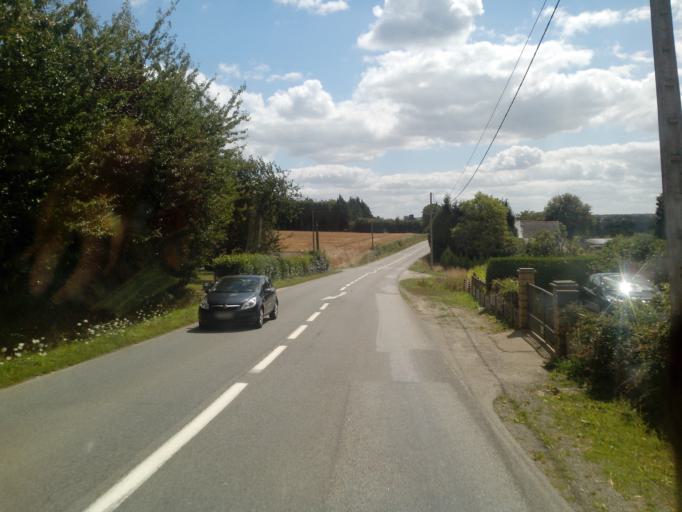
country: FR
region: Brittany
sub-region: Departement des Cotes-d'Armor
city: Plumieux
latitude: 48.0883
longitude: -2.5451
